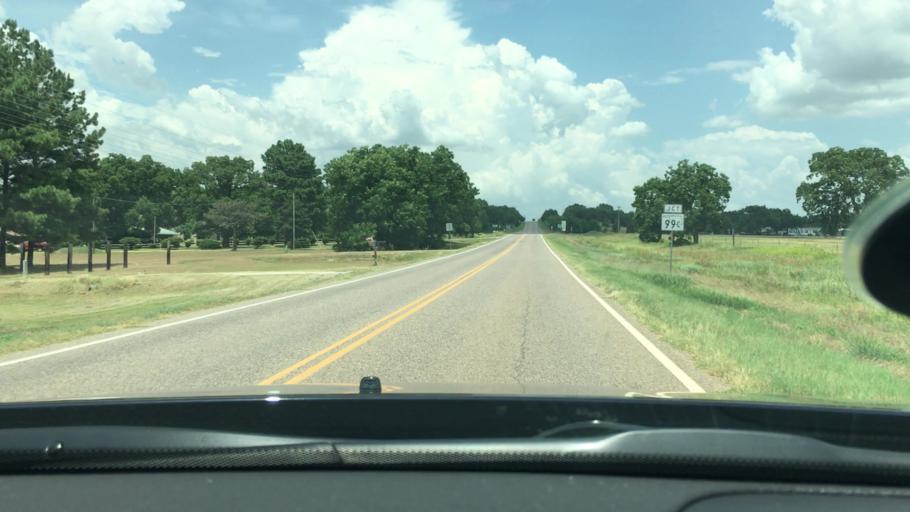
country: US
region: Oklahoma
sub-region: Marshall County
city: Oakland
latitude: 33.9929
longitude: -96.8820
